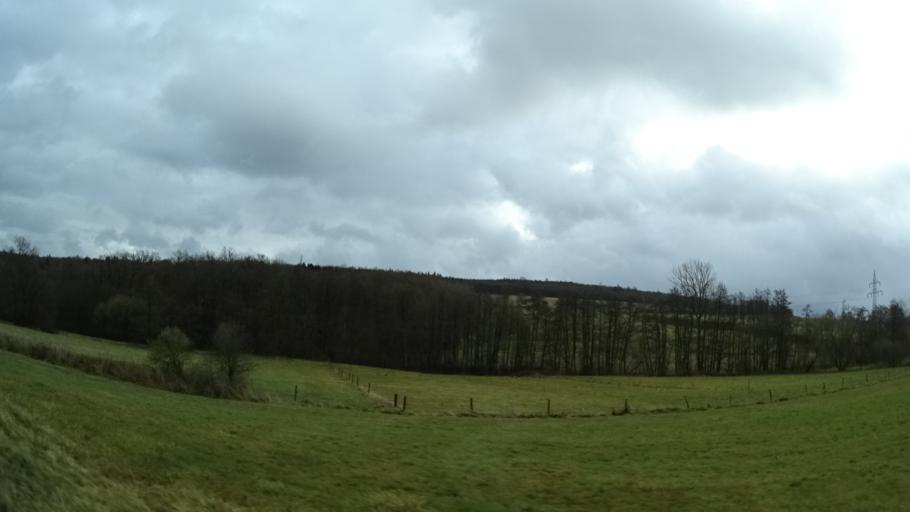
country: DE
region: Hesse
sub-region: Regierungsbezirk Giessen
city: Lautertal
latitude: 50.6133
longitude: 9.3134
